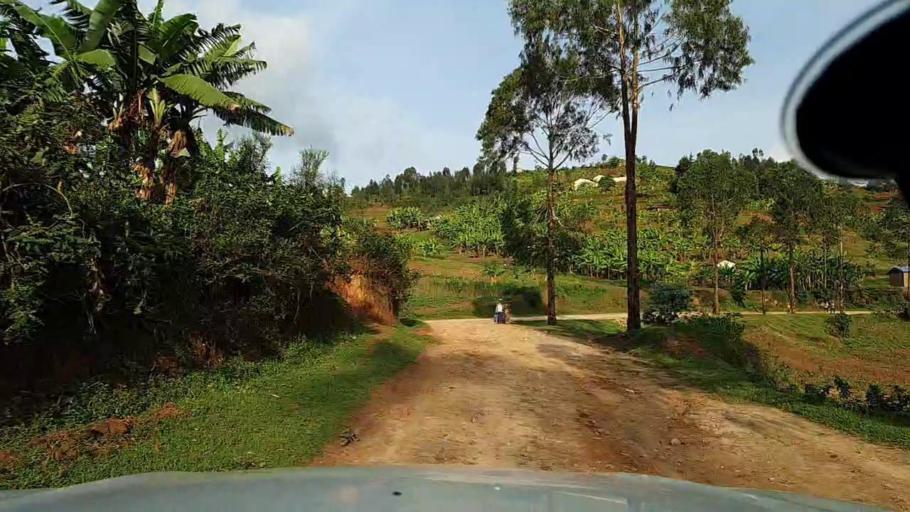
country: RW
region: Southern Province
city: Gitarama
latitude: -2.1819
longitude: 29.5619
